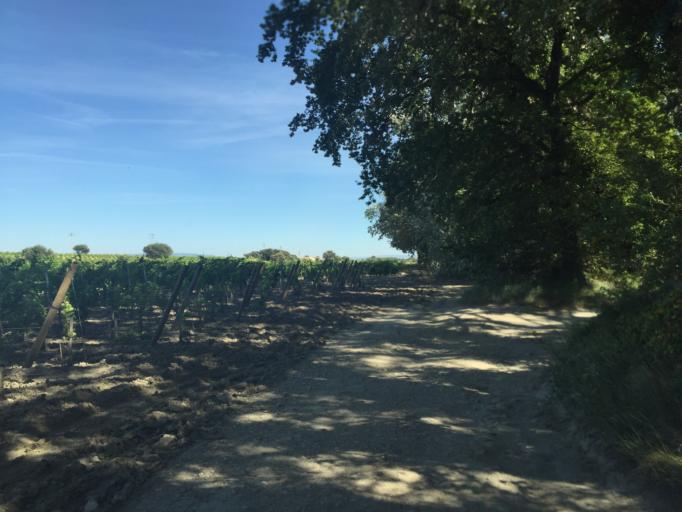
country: FR
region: Provence-Alpes-Cote d'Azur
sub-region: Departement du Vaucluse
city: Chateauneuf-du-Pape
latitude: 44.0414
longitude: 4.8266
